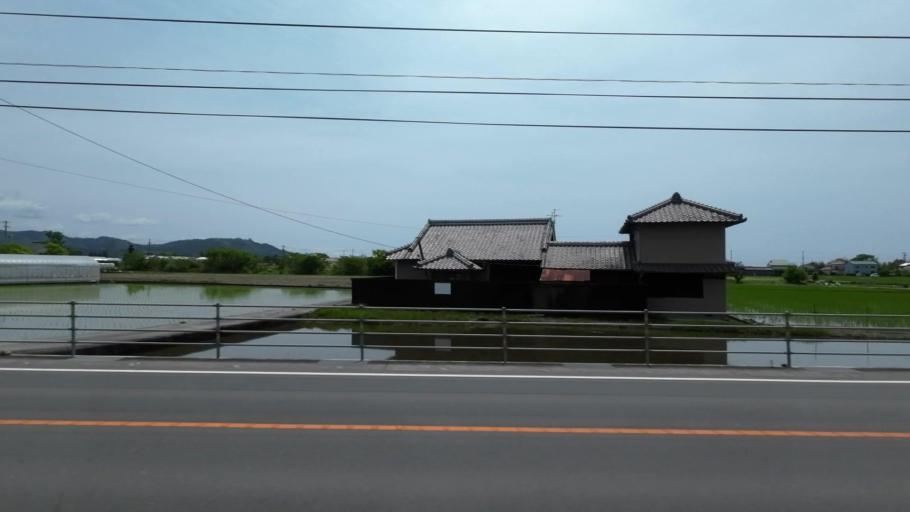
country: JP
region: Kochi
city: Kochi-shi
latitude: 33.5918
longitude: 133.6623
